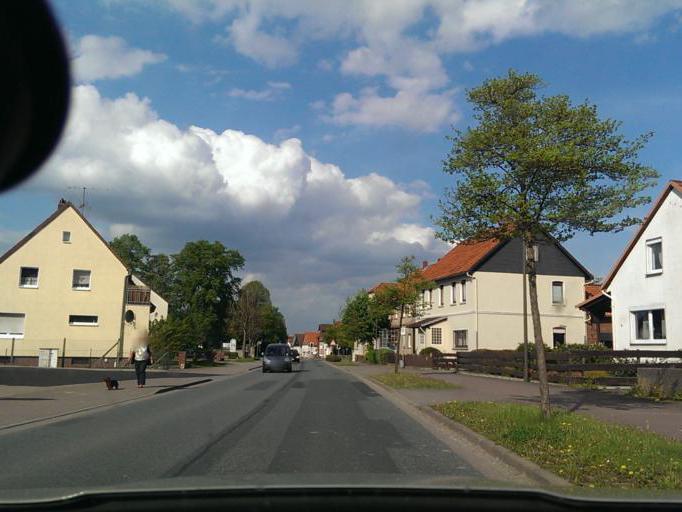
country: DE
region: Lower Saxony
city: Eime
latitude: 52.0735
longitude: 9.7195
